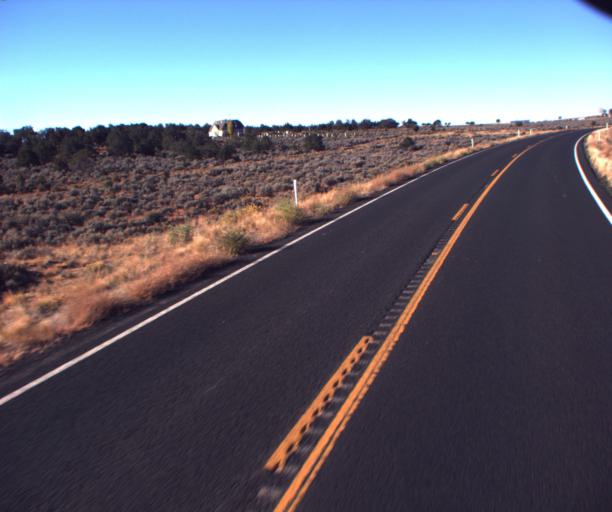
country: US
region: Arizona
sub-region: Apache County
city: Ganado
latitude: 35.7616
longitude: -109.7542
